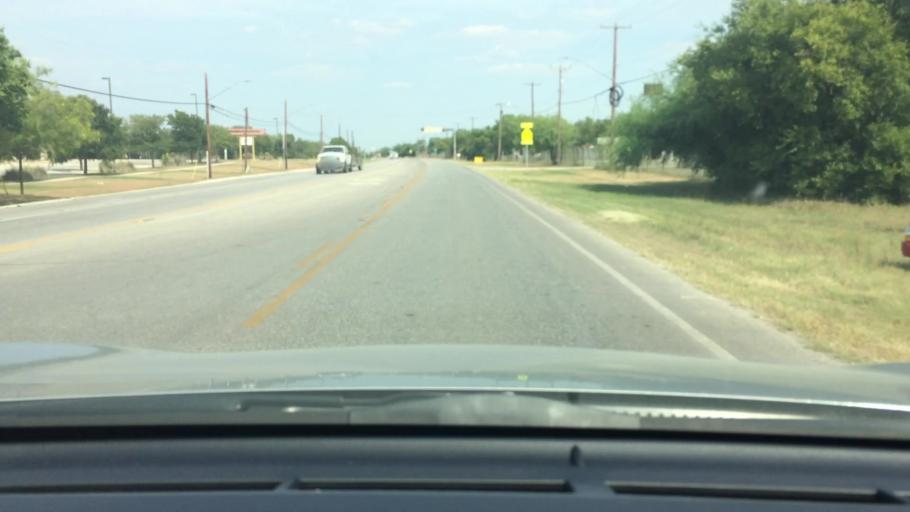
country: US
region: Texas
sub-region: Bexar County
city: San Antonio
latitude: 29.3296
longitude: -98.4419
